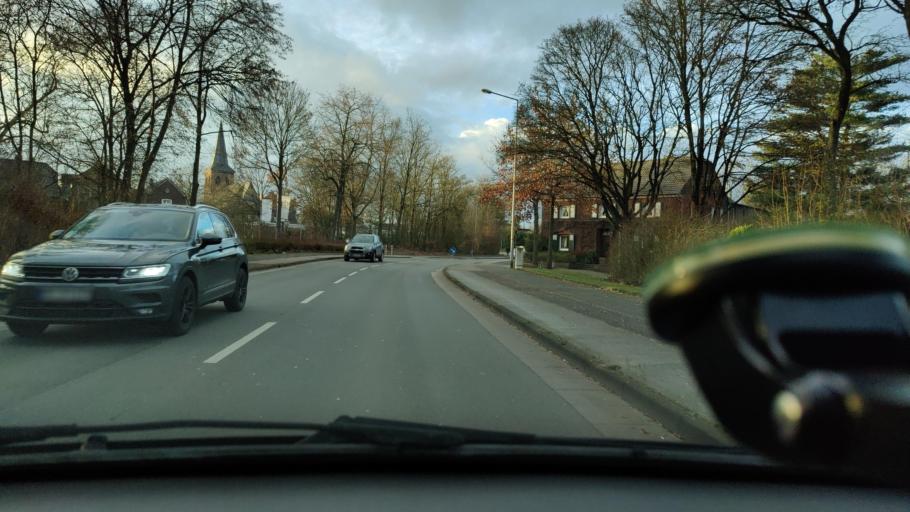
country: DE
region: North Rhine-Westphalia
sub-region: Regierungsbezirk Dusseldorf
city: Moers
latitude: 51.4882
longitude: 6.6117
